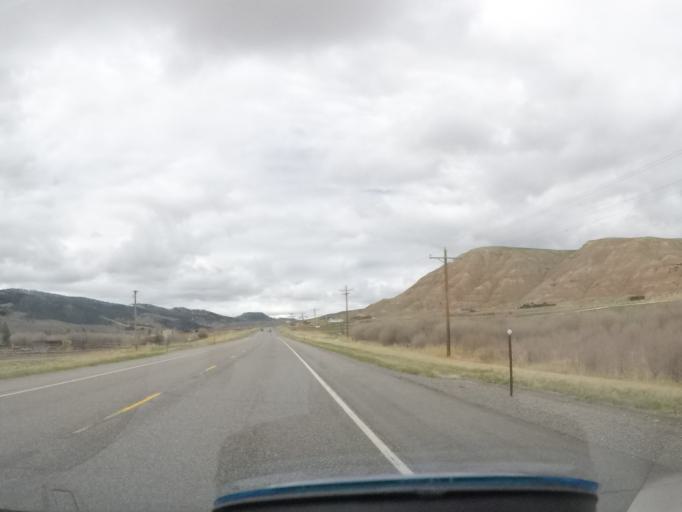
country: US
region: Wyoming
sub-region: Sublette County
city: Pinedale
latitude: 43.5682
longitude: -109.7111
